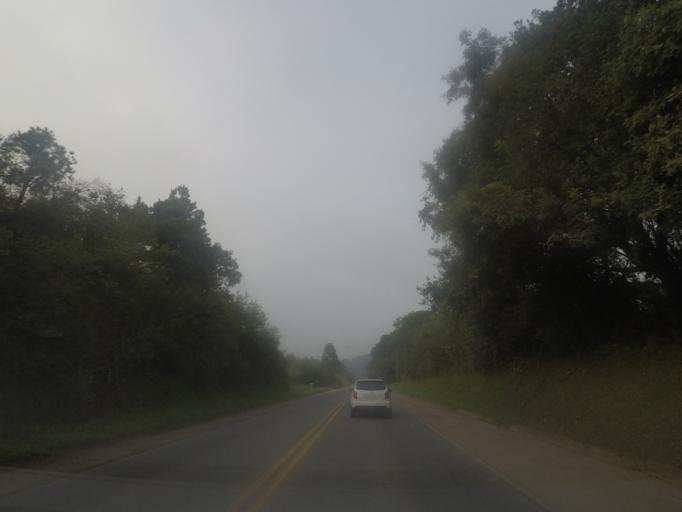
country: BR
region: Parana
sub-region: Almirante Tamandare
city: Almirante Tamandare
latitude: -25.2981
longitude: -49.3031
